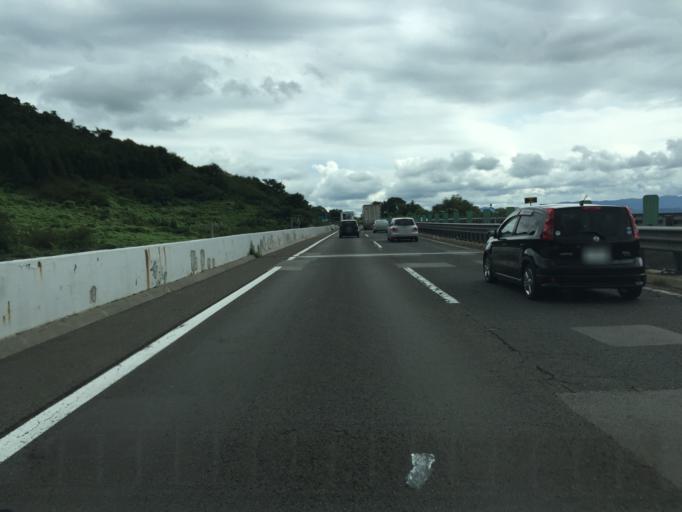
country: JP
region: Fukushima
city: Yanagawamachi-saiwaicho
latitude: 37.8918
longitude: 140.5603
